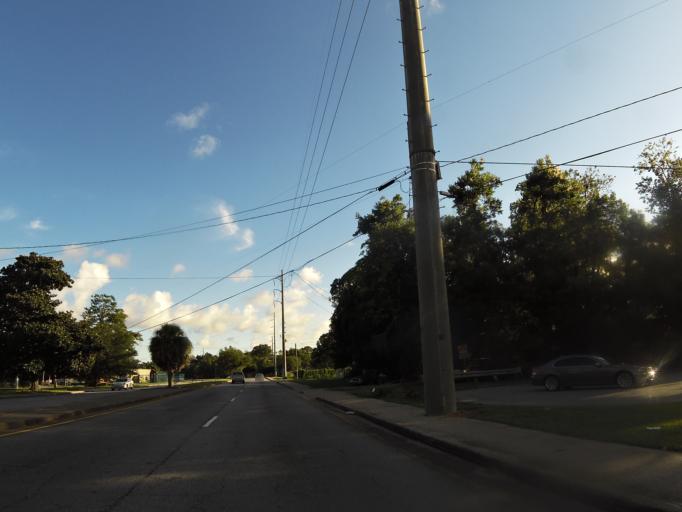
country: US
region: Georgia
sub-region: Glynn County
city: Brunswick
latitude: 31.1680
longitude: -81.4928
